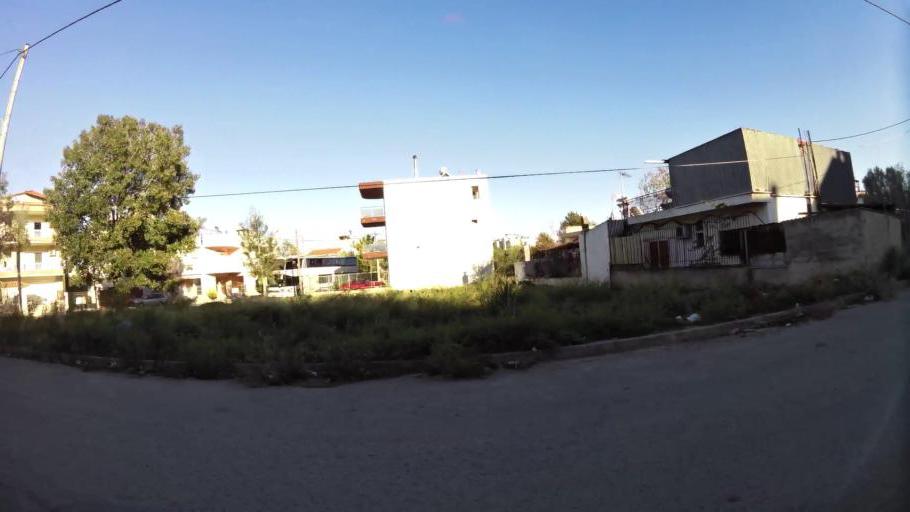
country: GR
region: Attica
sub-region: Nomarchia Anatolikis Attikis
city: Acharnes
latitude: 38.0772
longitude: 23.7264
